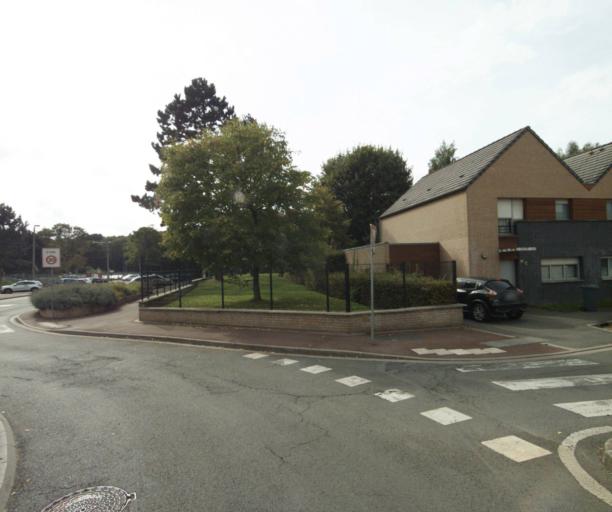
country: FR
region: Nord-Pas-de-Calais
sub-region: Departement du Nord
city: Lomme
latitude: 50.6493
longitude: 2.9977
